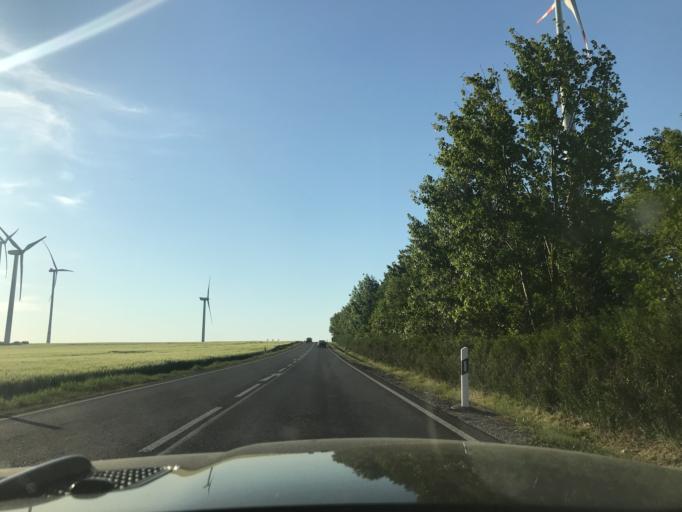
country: DE
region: Thuringia
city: Hochheim
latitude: 51.0360
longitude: 10.6678
